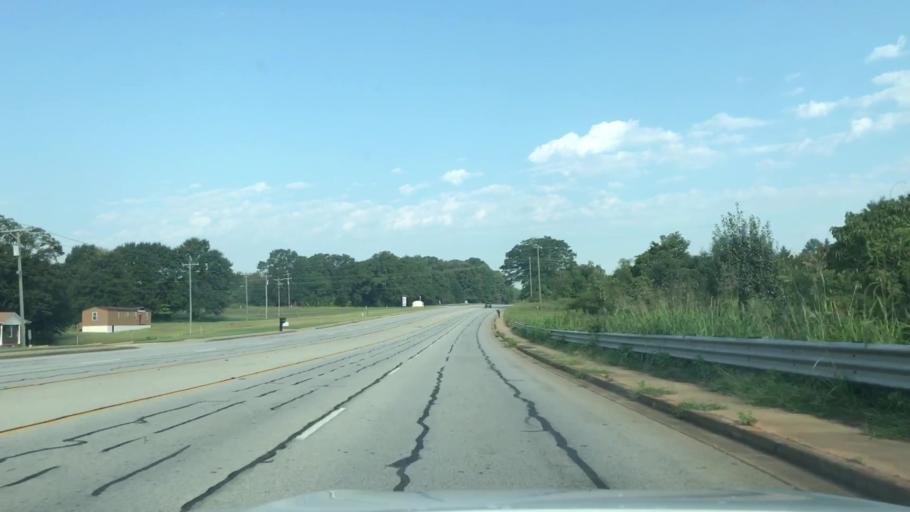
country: US
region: South Carolina
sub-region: Spartanburg County
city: Wellford
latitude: 34.8805
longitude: -82.0563
